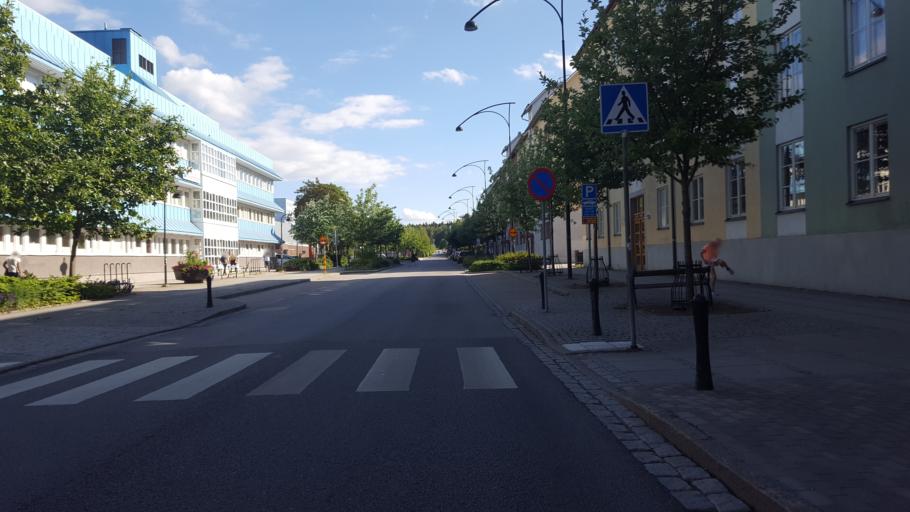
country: SE
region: Stockholm
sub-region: Upplands Vasby Kommun
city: Upplands Vaesby
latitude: 59.5202
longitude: 17.9091
